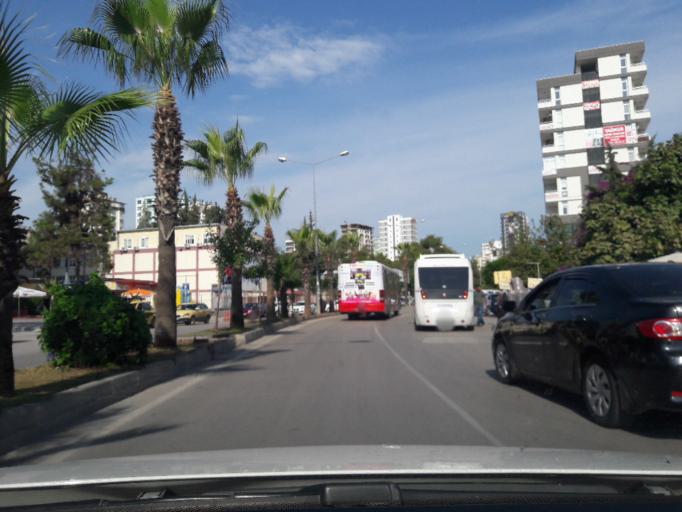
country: TR
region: Adana
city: Adana
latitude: 37.0198
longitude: 35.3201
